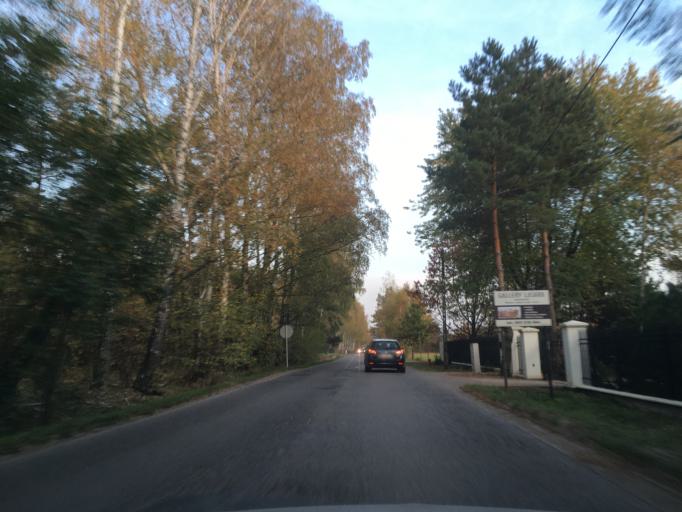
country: PL
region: Masovian Voivodeship
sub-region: Powiat piaseczynski
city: Lesznowola
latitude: 52.0590
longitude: 20.9152
